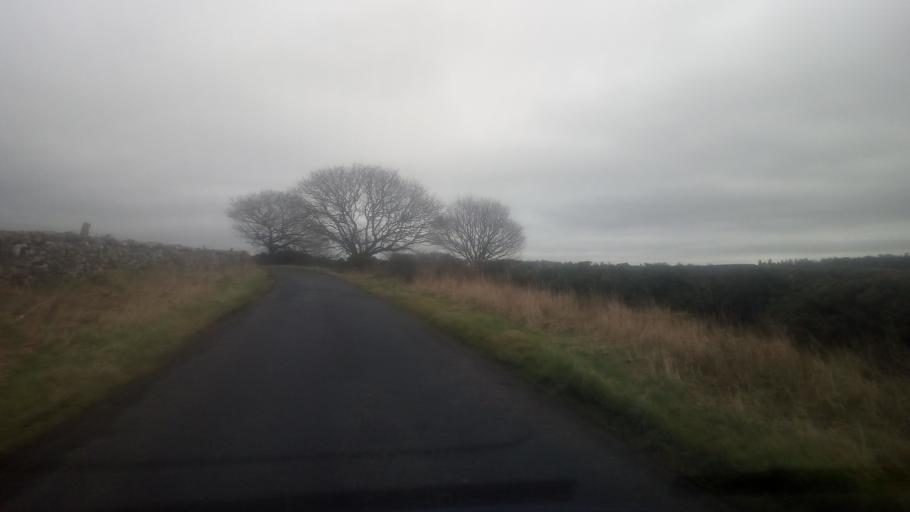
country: GB
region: Scotland
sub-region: The Scottish Borders
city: Kelso
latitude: 55.5504
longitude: -2.4874
